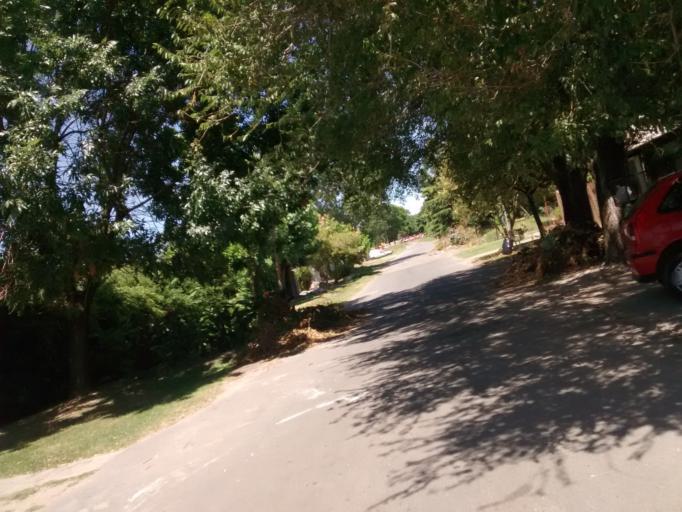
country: AR
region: Buenos Aires
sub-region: Partido de La Plata
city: La Plata
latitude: -34.8812
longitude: -58.0032
